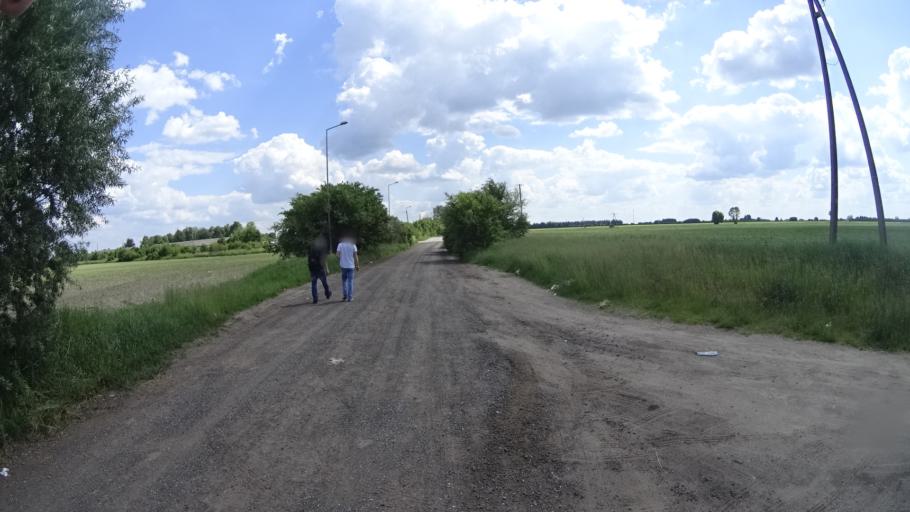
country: PL
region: Masovian Voivodeship
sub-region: Powiat pruszkowski
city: Nadarzyn
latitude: 52.0561
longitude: 20.8241
